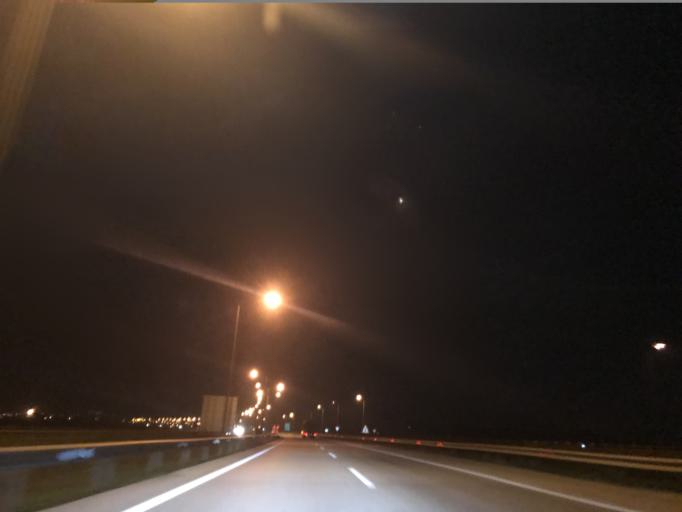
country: TR
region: Hatay
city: Mahmutlar
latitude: 36.9609
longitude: 36.1215
